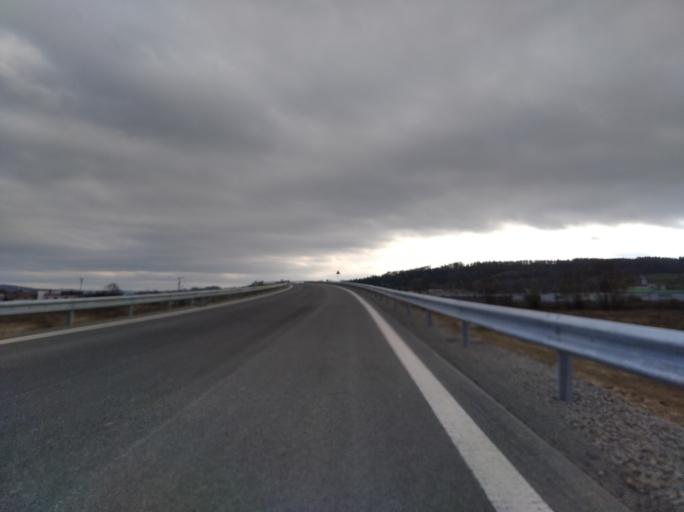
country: PL
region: Subcarpathian Voivodeship
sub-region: Powiat strzyzowski
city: Strzyzow
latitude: 49.8708
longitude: 21.7670
